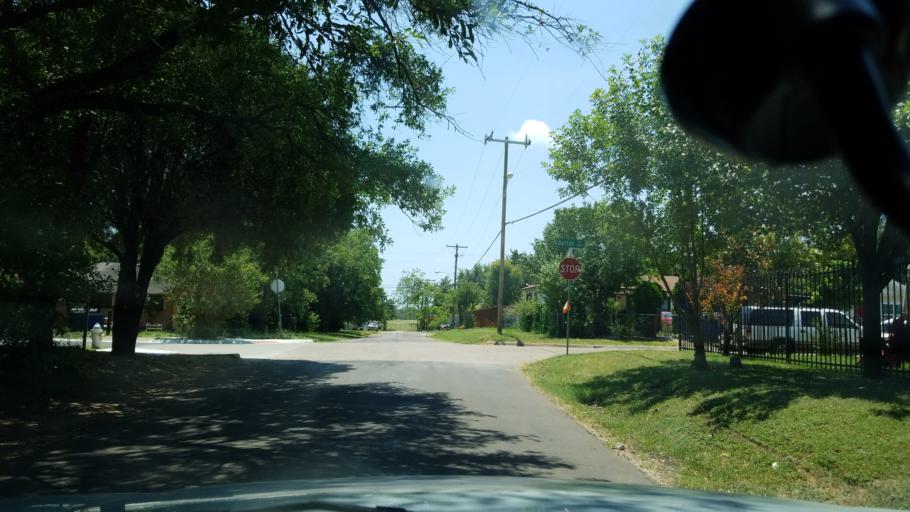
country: US
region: Texas
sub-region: Dallas County
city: Cockrell Hill
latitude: 32.7256
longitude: -96.8661
